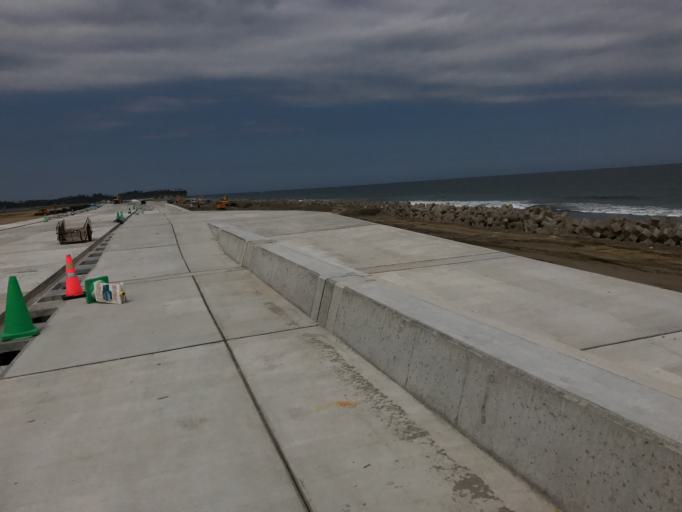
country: JP
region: Miyagi
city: Marumori
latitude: 37.8025
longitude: 140.9859
